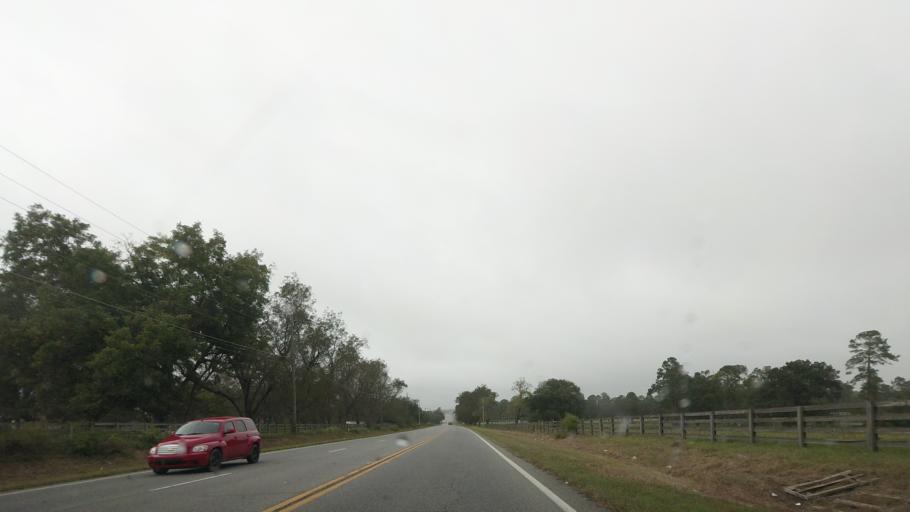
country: US
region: Georgia
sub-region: Ben Hill County
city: Fitzgerald
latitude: 31.6841
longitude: -83.2388
